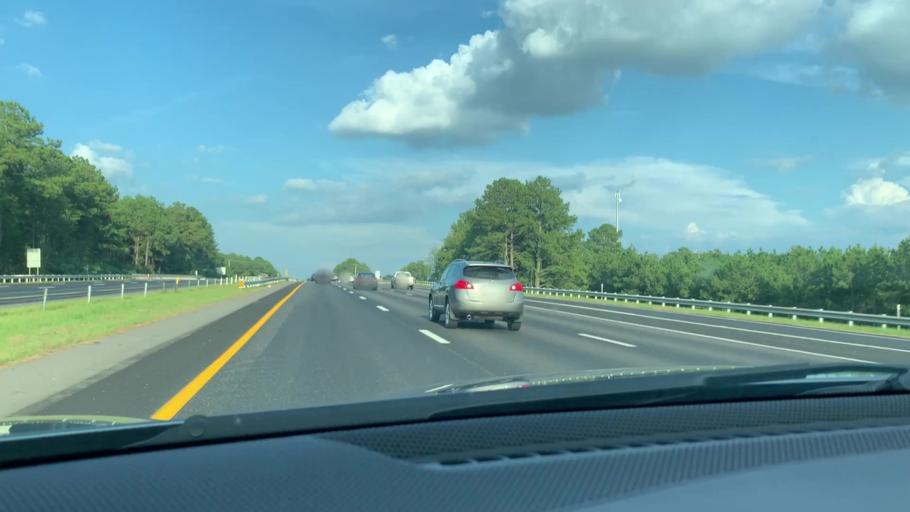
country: US
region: South Carolina
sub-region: Richland County
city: Forest Acres
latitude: 33.9523
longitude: -80.9660
